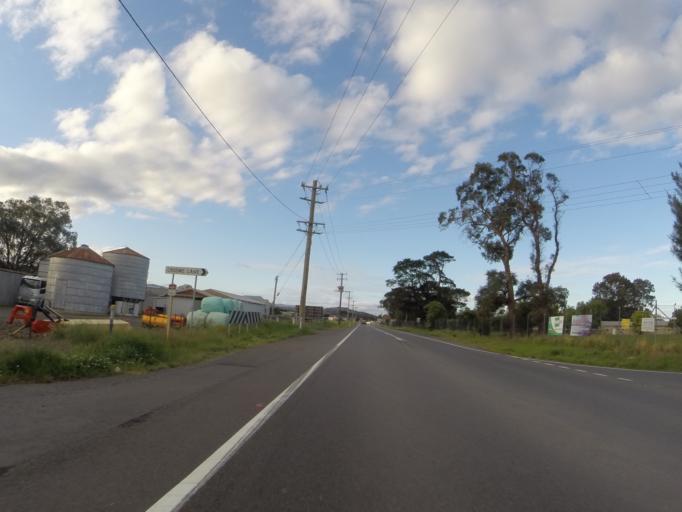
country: AU
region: New South Wales
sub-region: Shellharbour
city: Albion Park Rail
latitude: -34.5527
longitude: 150.7823
